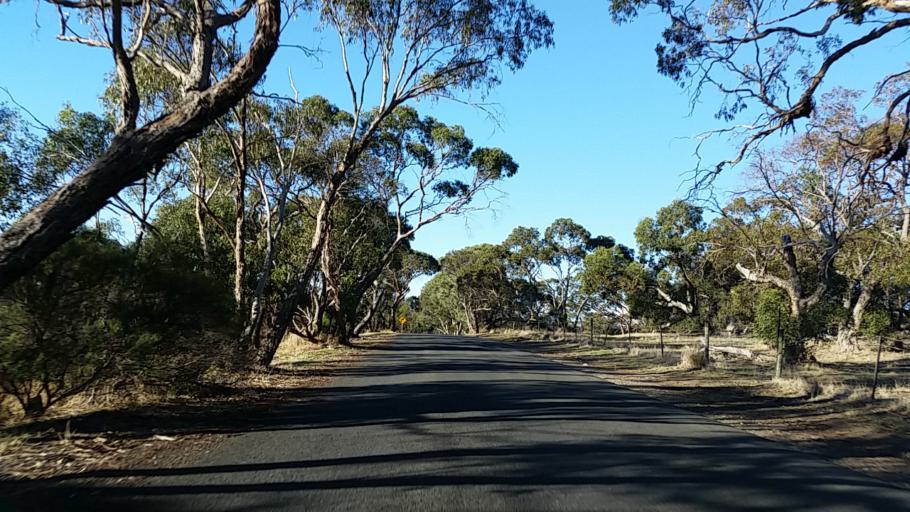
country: AU
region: South Australia
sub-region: Onkaparinga
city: Hackham
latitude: -35.1560
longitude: 138.5462
